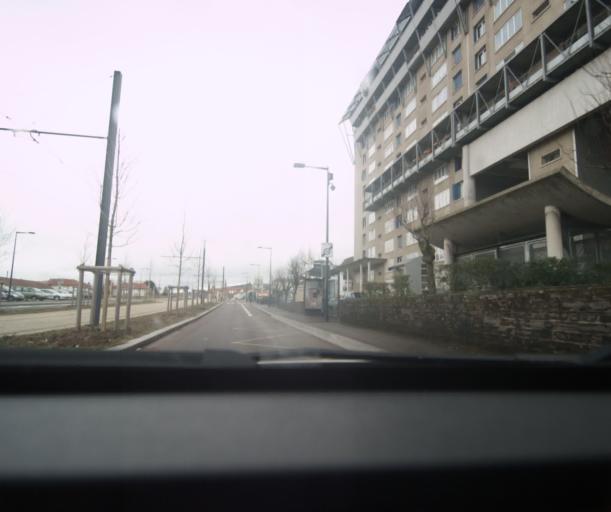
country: FR
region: Franche-Comte
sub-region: Departement du Doubs
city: Beure
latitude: 47.2285
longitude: 6.0062
